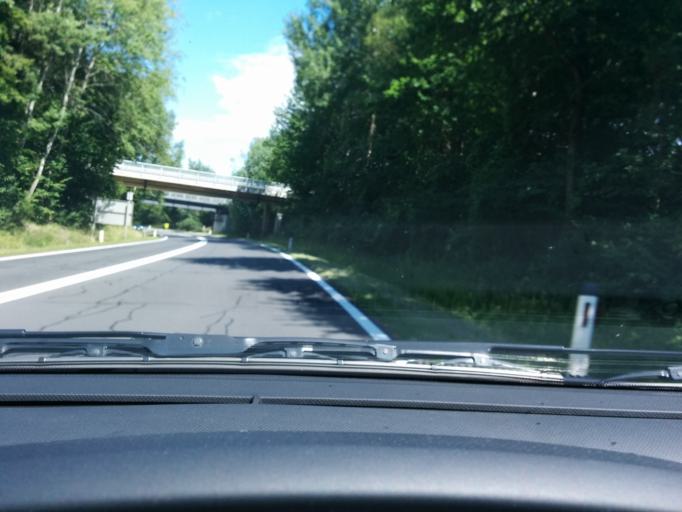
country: AT
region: Styria
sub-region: Politischer Bezirk Hartberg-Fuerstenfeld
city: Grafendorf bei Hartberg
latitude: 47.3407
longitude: 16.0042
